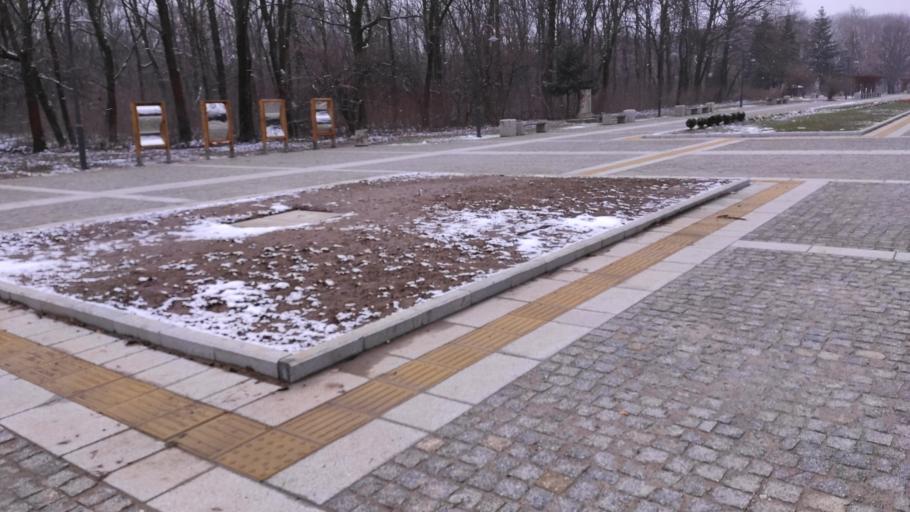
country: BG
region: Sofia-Capital
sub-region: Stolichna Obshtina
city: Sofia
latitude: 42.7117
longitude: 23.2815
